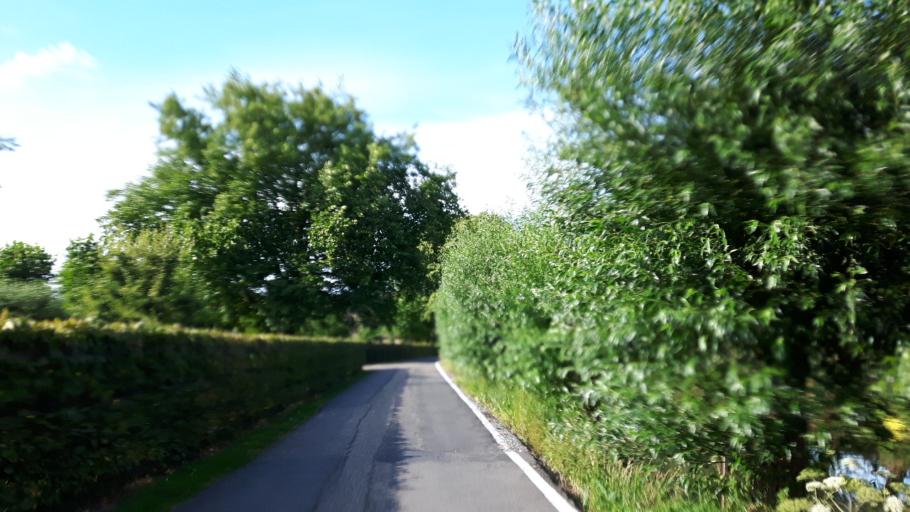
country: NL
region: Utrecht
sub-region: Gemeente Oudewater
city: Oudewater
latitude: 52.0307
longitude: 4.8833
